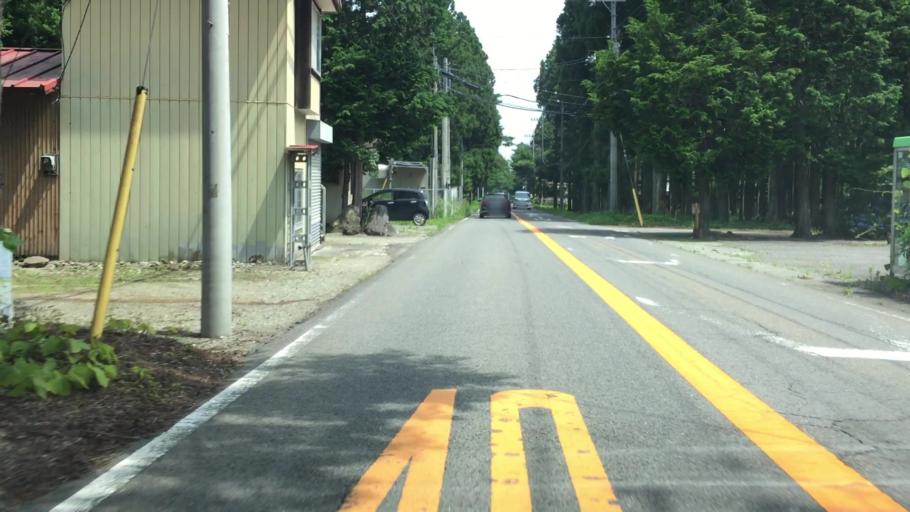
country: JP
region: Tochigi
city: Kuroiso
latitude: 37.0487
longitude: 139.9358
